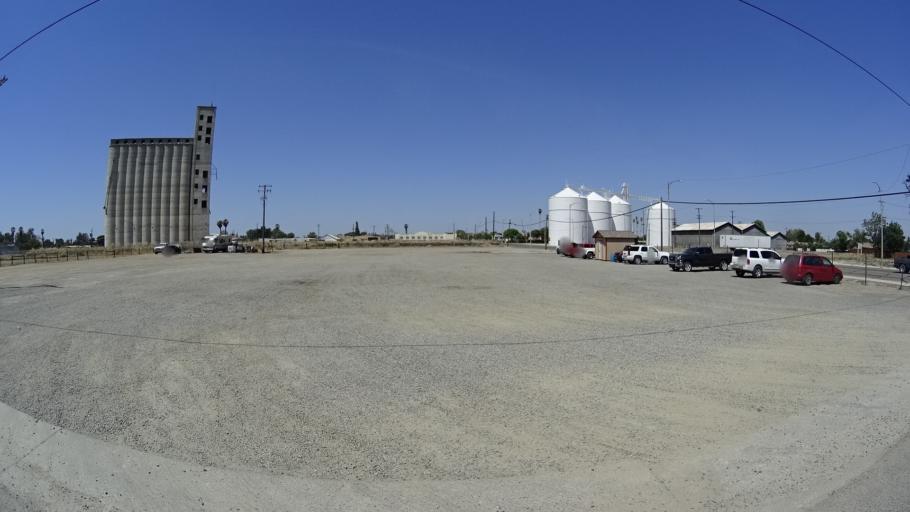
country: US
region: California
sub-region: Kings County
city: Corcoran
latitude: 36.0978
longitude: -119.5543
